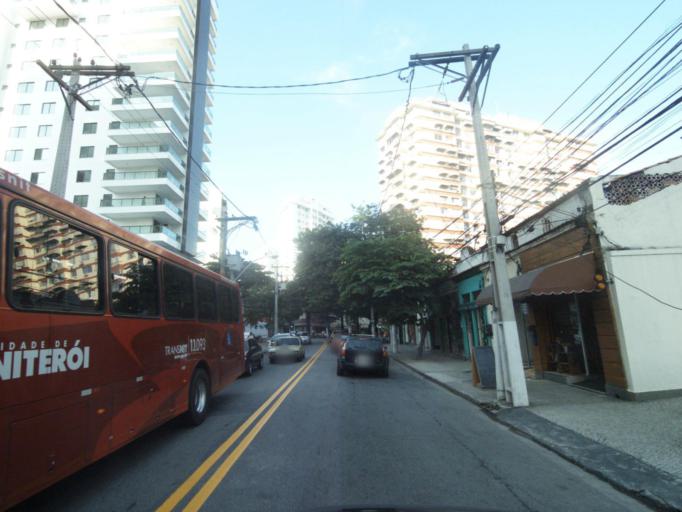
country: BR
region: Rio de Janeiro
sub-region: Niteroi
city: Niteroi
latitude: -22.8973
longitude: -43.1016
